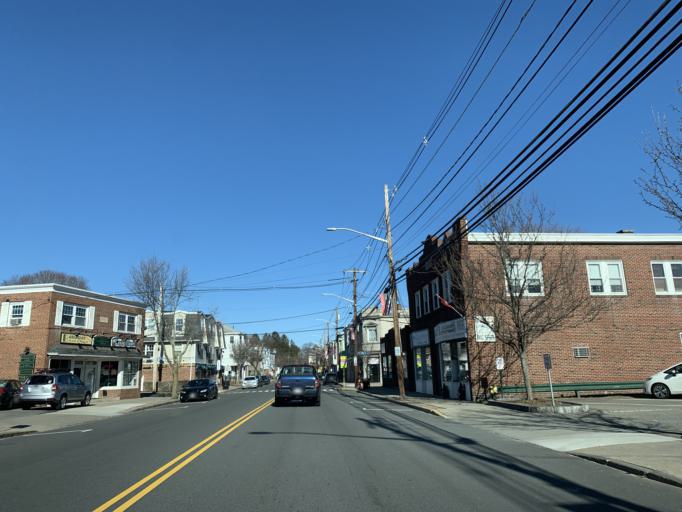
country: US
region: Massachusetts
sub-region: Norfolk County
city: Norwood
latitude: 42.1775
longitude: -71.2062
